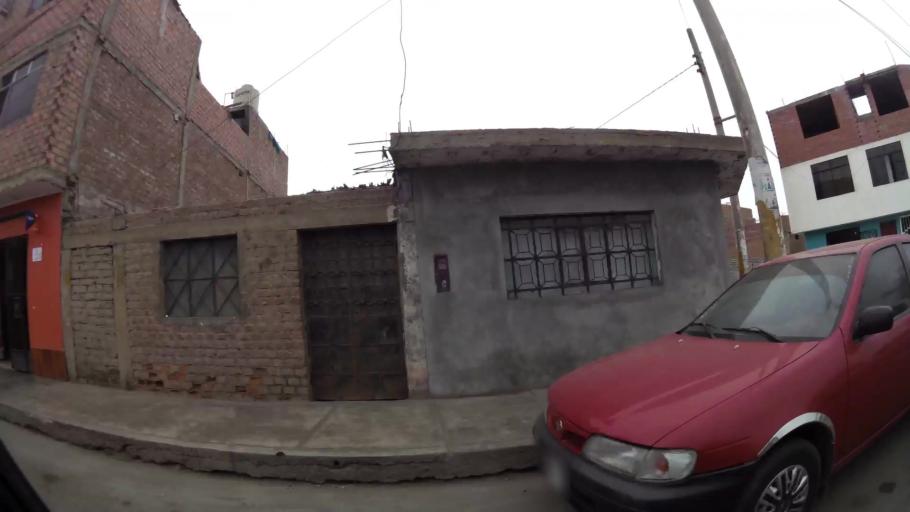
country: PE
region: Lima
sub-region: Barranca
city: Barranca
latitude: -10.7496
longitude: -77.7537
